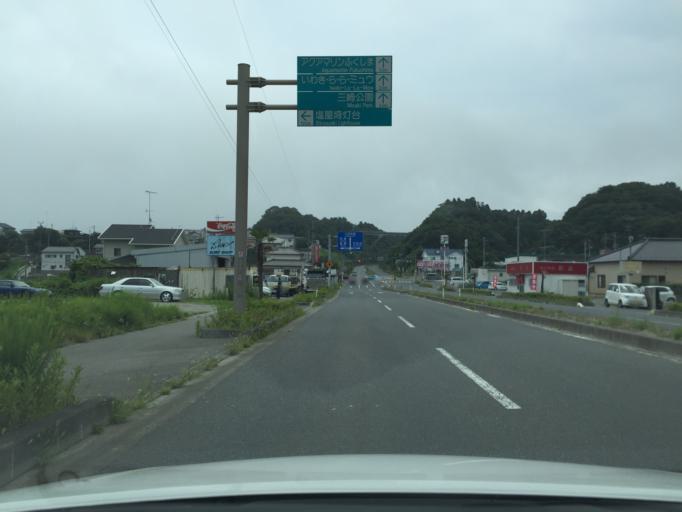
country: JP
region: Fukushima
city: Iwaki
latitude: 36.9512
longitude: 140.9212
